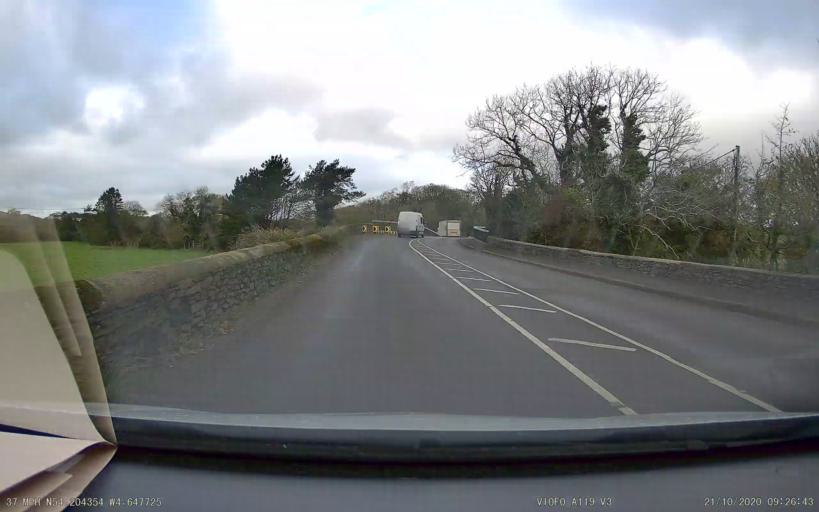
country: IM
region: Castletown
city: Castletown
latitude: 54.2043
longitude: -4.6478
